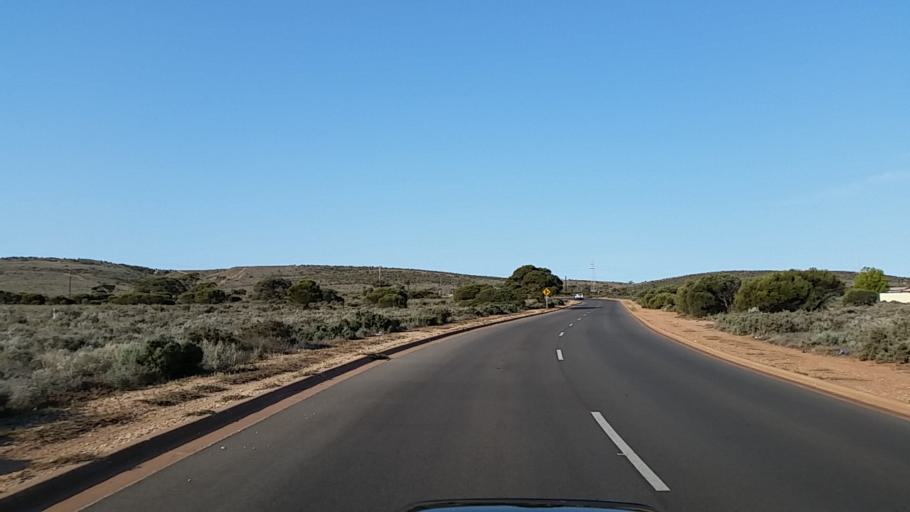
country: AU
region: South Australia
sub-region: Whyalla
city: Whyalla
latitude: -33.0091
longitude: 137.5291
